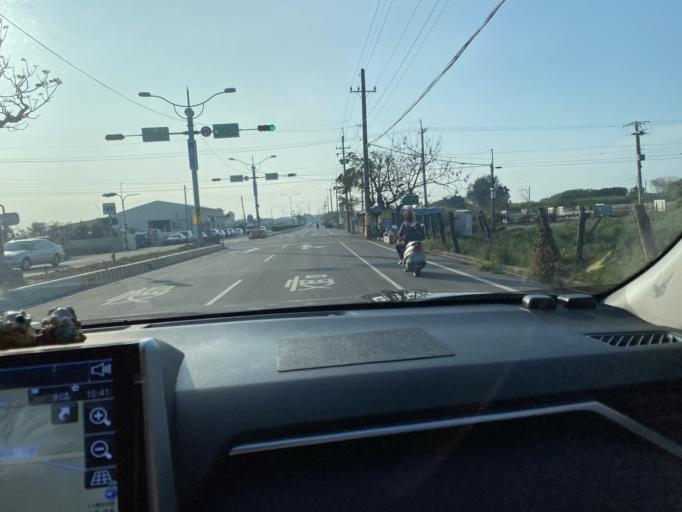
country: TW
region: Taiwan
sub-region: Changhua
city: Chang-hua
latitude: 23.9597
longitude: 120.3689
